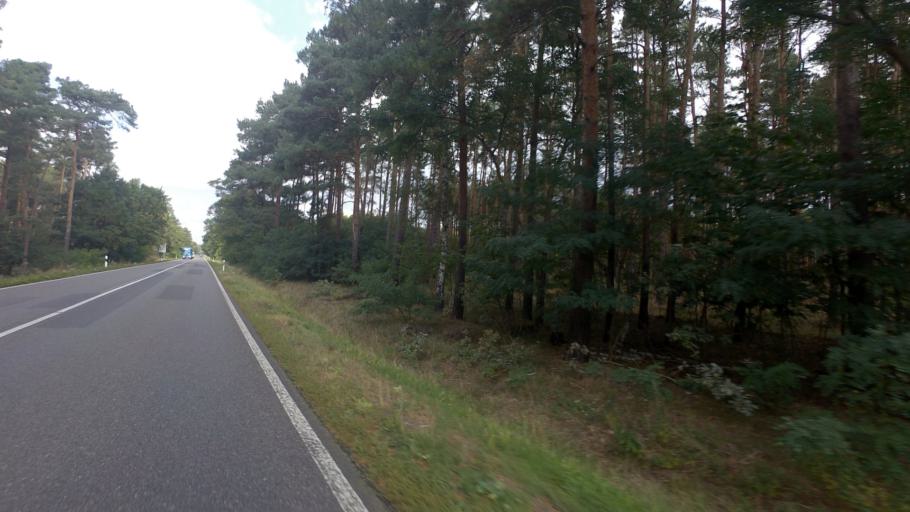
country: DE
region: Saxony-Anhalt
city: Holzdorf
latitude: 51.7731
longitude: 13.1974
